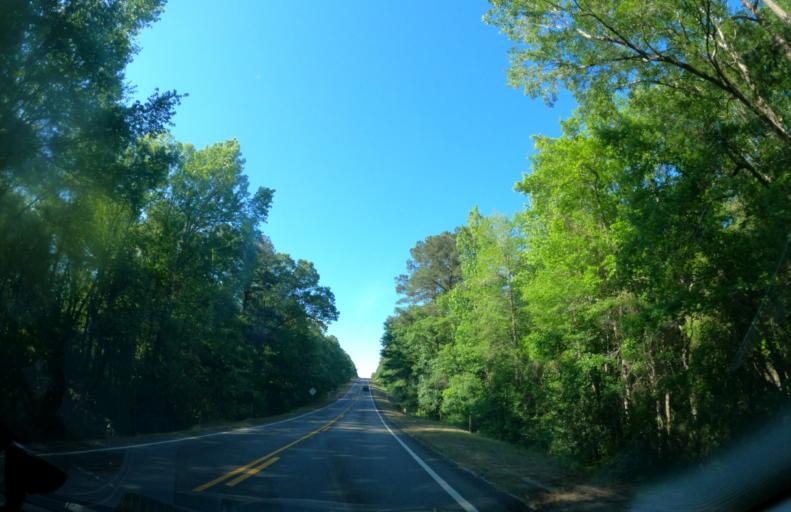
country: US
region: Georgia
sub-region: Columbia County
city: Harlem
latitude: 33.3675
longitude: -82.3240
